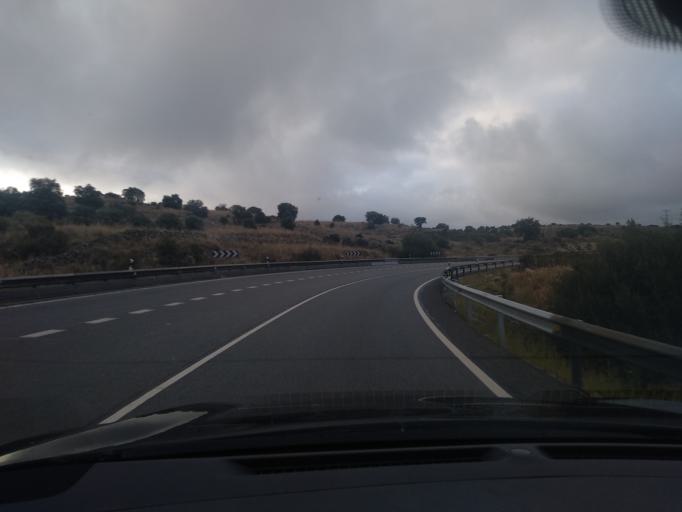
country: ES
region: Castille and Leon
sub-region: Provincia de Segovia
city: Otero de Herreros
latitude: 40.7716
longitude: -4.2013
